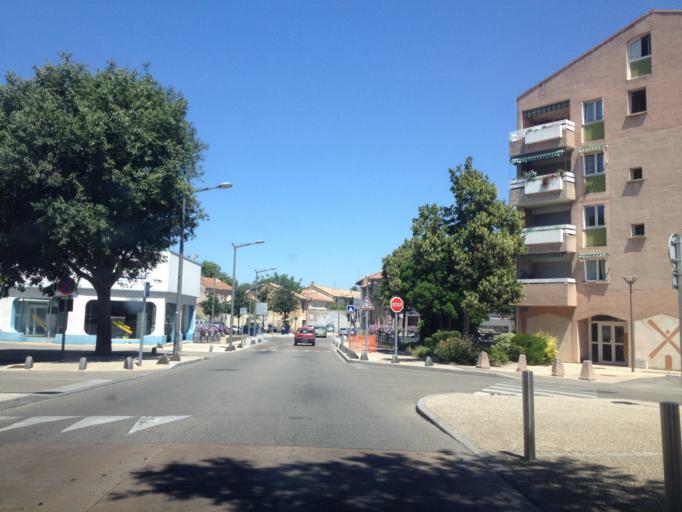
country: FR
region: Provence-Alpes-Cote d'Azur
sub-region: Departement du Vaucluse
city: Sorgues
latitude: 44.0094
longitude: 4.8715
